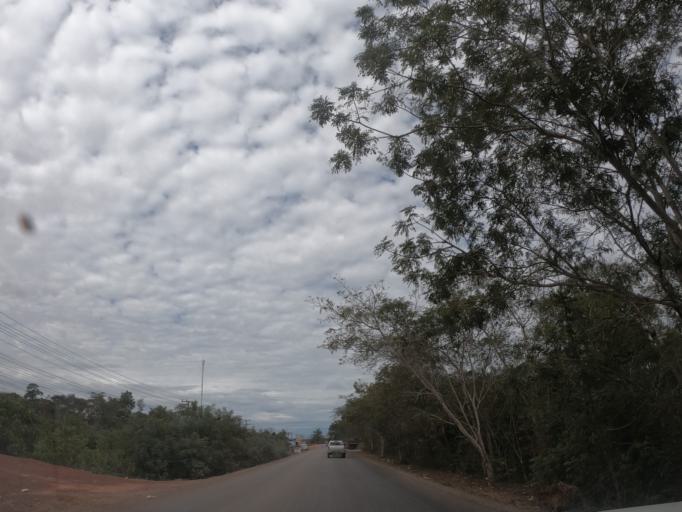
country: TH
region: Nakhon Phanom
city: Nakhon Phanom
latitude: 17.5232
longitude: 104.7260
